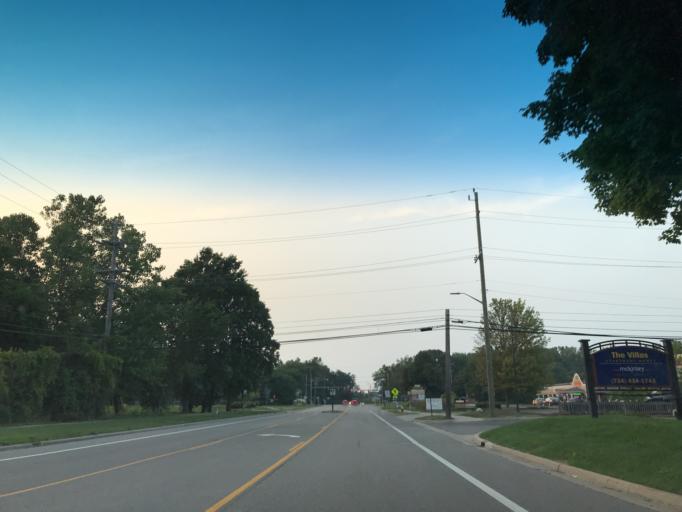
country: US
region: Michigan
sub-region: Washtenaw County
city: Ypsilanti
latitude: 42.2571
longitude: -83.6612
